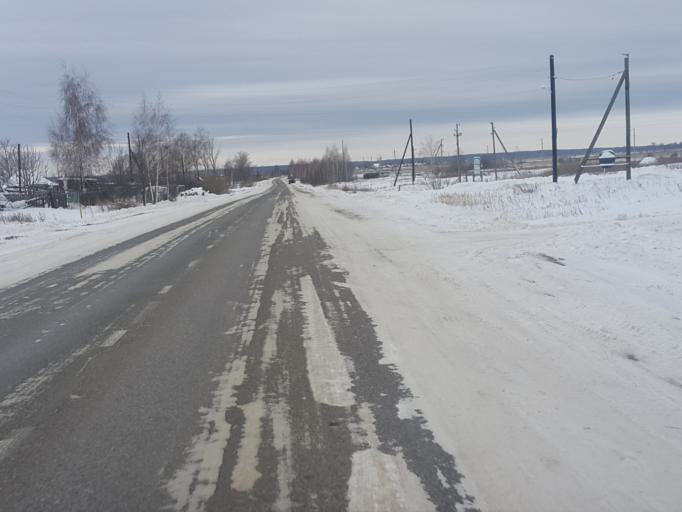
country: RU
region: Tambov
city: Platonovka
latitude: 52.8609
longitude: 41.8411
